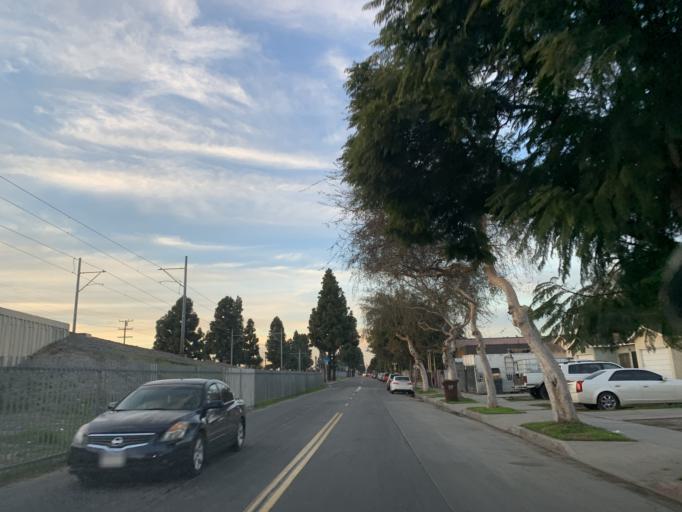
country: US
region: California
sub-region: Los Angeles County
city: Compton
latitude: 33.9078
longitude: -118.2268
